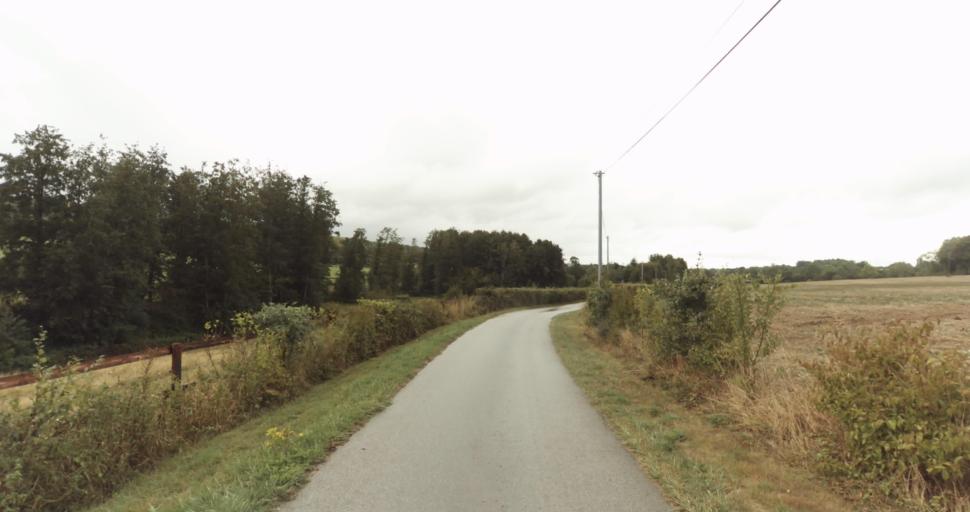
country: FR
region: Lower Normandy
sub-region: Departement de l'Orne
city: Sainte-Gauburge-Sainte-Colombe
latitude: 48.6974
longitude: 0.4290
